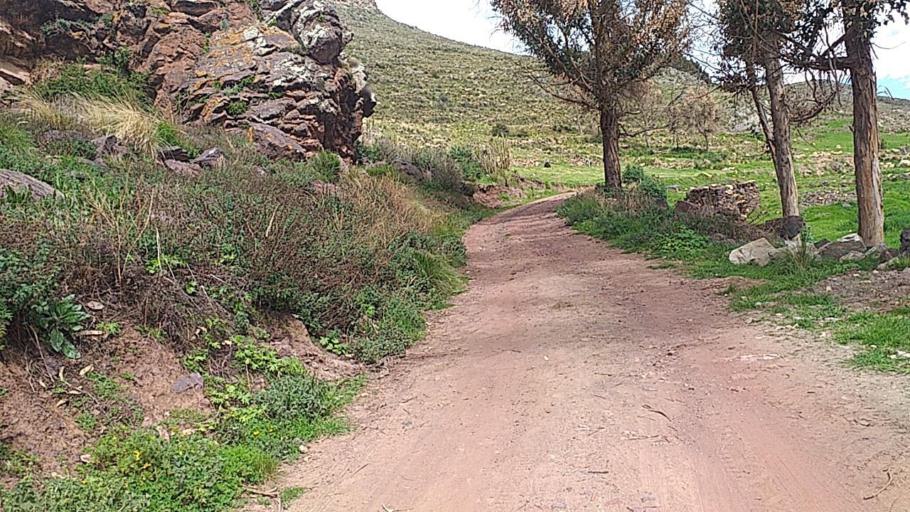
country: BO
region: La Paz
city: Batallas
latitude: -16.3426
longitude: -68.6352
